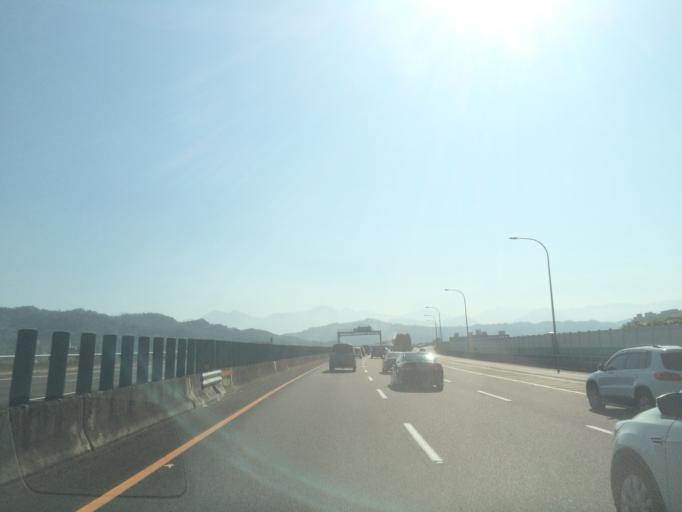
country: TW
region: Taiwan
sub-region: Nantou
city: Nantou
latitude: 23.9188
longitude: 120.6892
